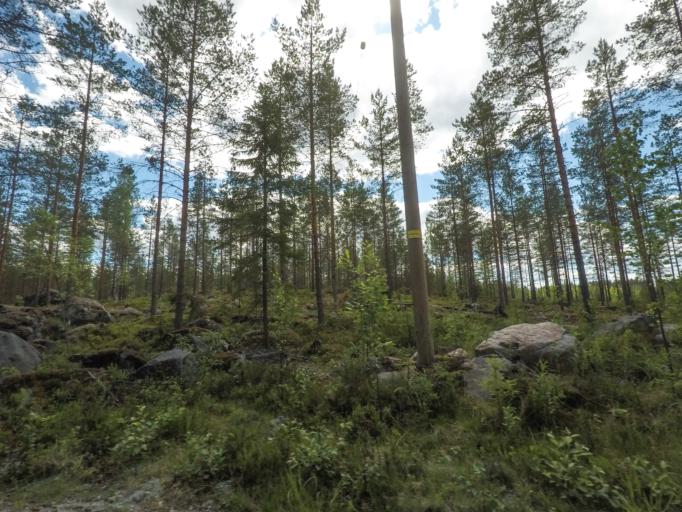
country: FI
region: Central Finland
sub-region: Jyvaeskylae
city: Hankasalmi
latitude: 62.4054
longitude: 26.6567
